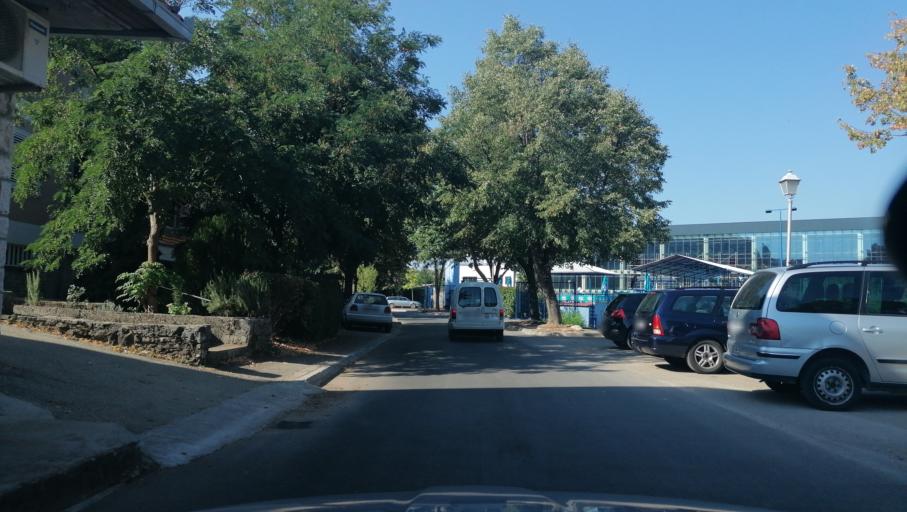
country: BA
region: Republika Srpska
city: Trebinje
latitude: 42.7143
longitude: 18.3498
